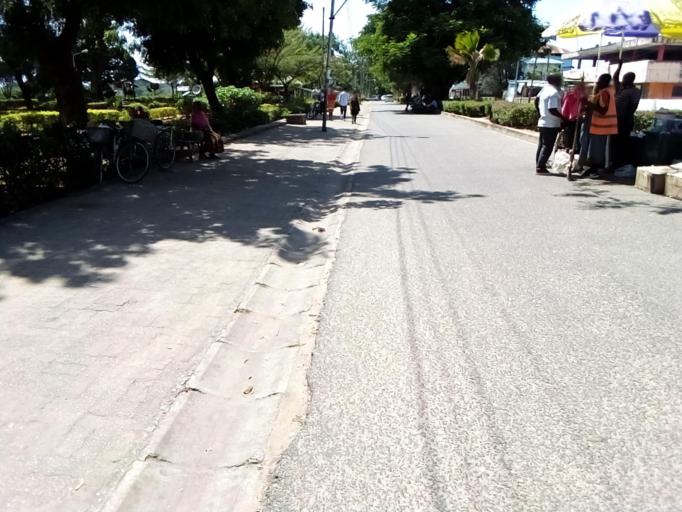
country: TZ
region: Tanga
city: Tanga
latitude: -5.0703
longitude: 39.1002
